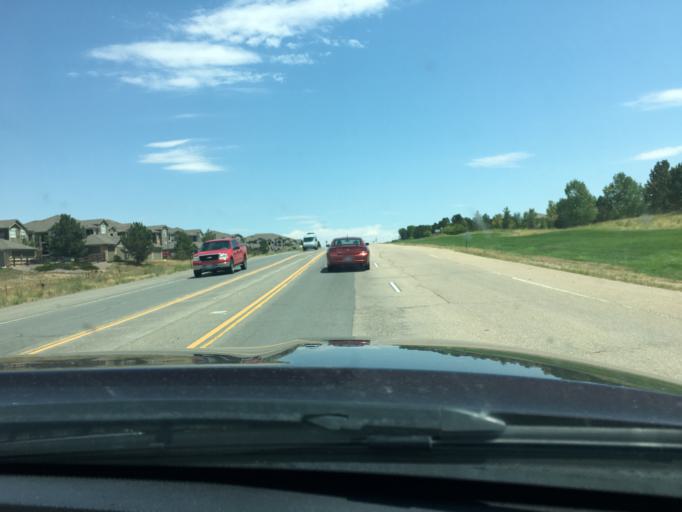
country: US
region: Colorado
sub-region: Boulder County
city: Erie
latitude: 40.0005
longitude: -105.0325
